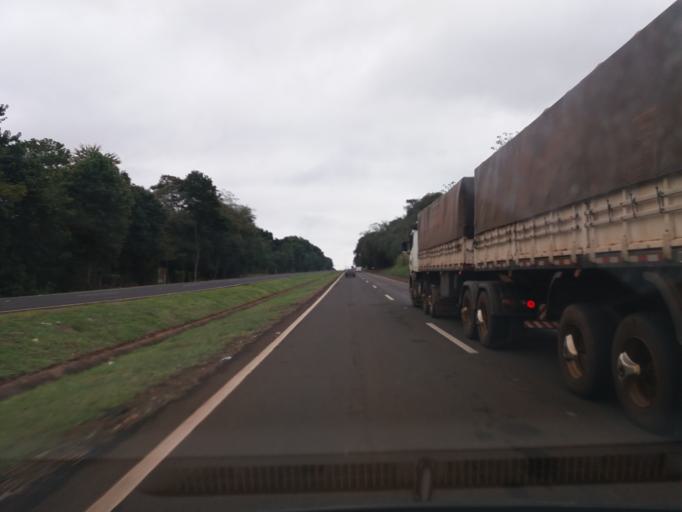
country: BR
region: Parana
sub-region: Paicandu
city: Paicandu
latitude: -23.5036
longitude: -52.0192
